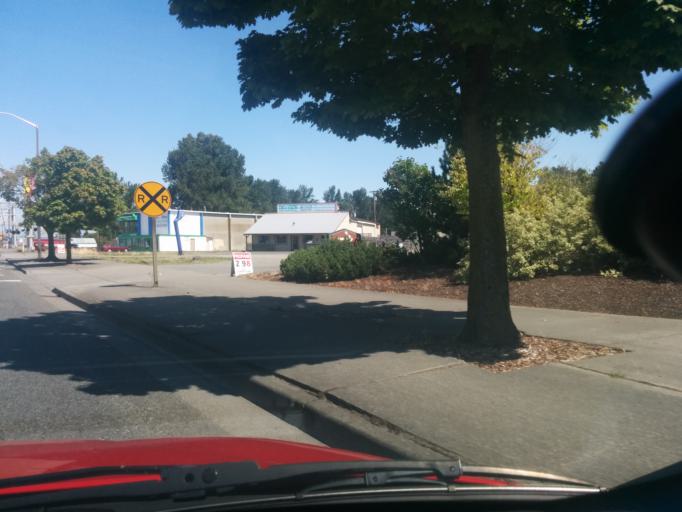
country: US
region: Washington
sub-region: Skagit County
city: Mount Vernon
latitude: 48.4292
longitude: -122.3352
